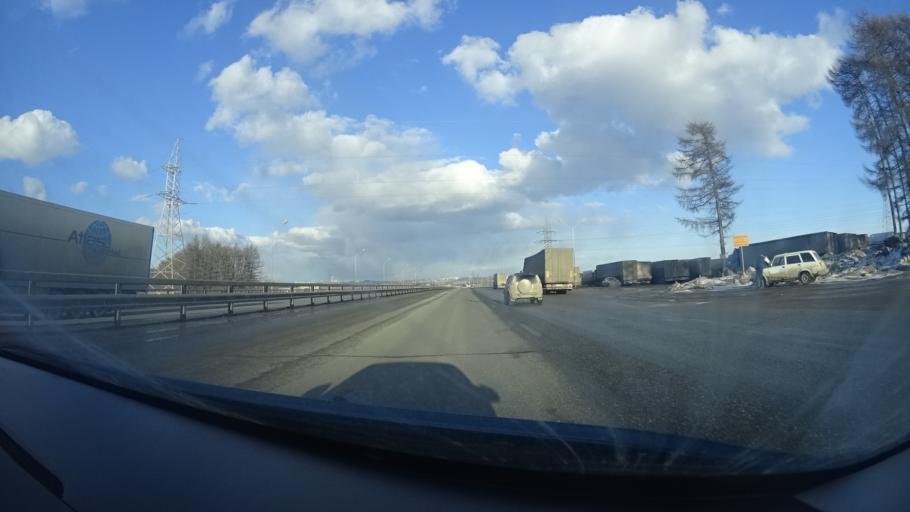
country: RU
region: Bashkortostan
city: Avdon
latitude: 54.6739
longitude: 55.7859
